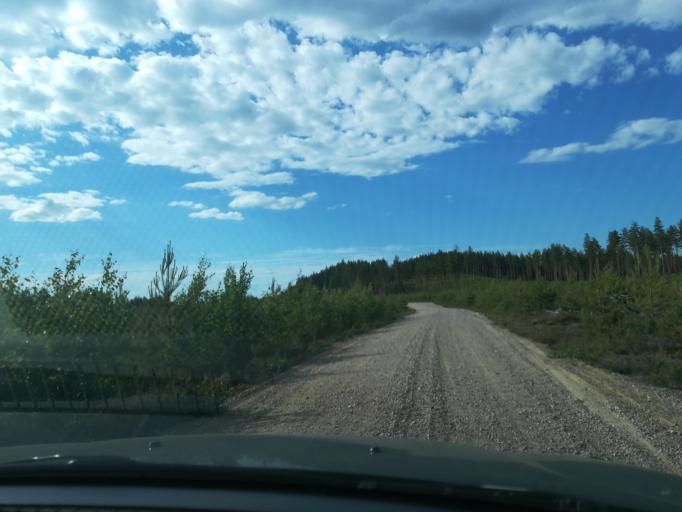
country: FI
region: Southern Savonia
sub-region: Savonlinna
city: Savonlinna
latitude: 61.6375
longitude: 28.7270
